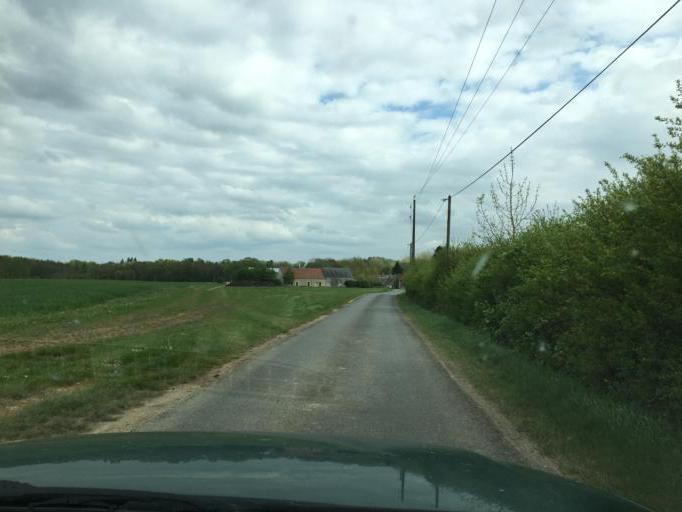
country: FR
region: Centre
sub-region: Departement du Loiret
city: Meung-sur-Loire
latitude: 47.8626
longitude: 1.6797
